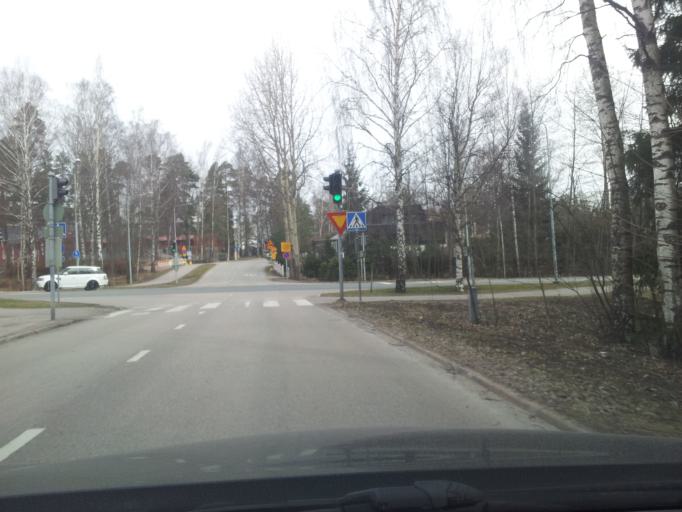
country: FI
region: Uusimaa
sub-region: Helsinki
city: Kilo
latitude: 60.2007
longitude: 24.8040
